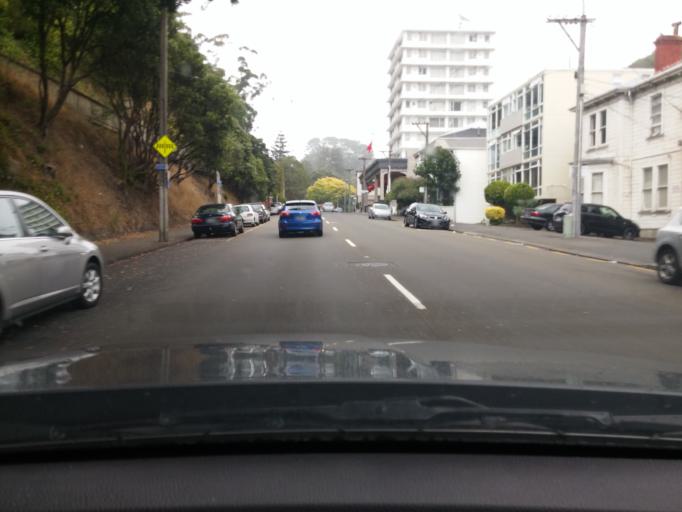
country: NZ
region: Wellington
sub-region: Wellington City
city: Kelburn
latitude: -41.2795
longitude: 174.7685
